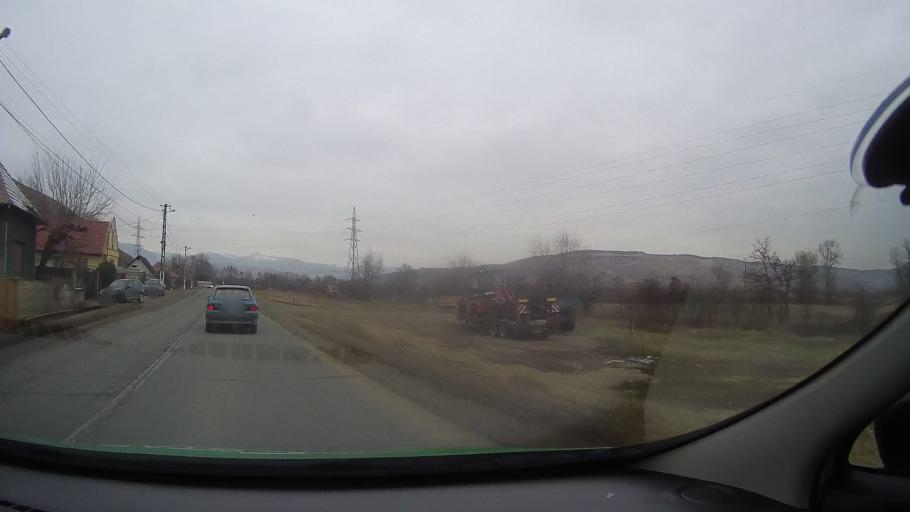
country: RO
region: Alba
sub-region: Comuna Ighiu
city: Sard
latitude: 46.1187
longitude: 23.5362
